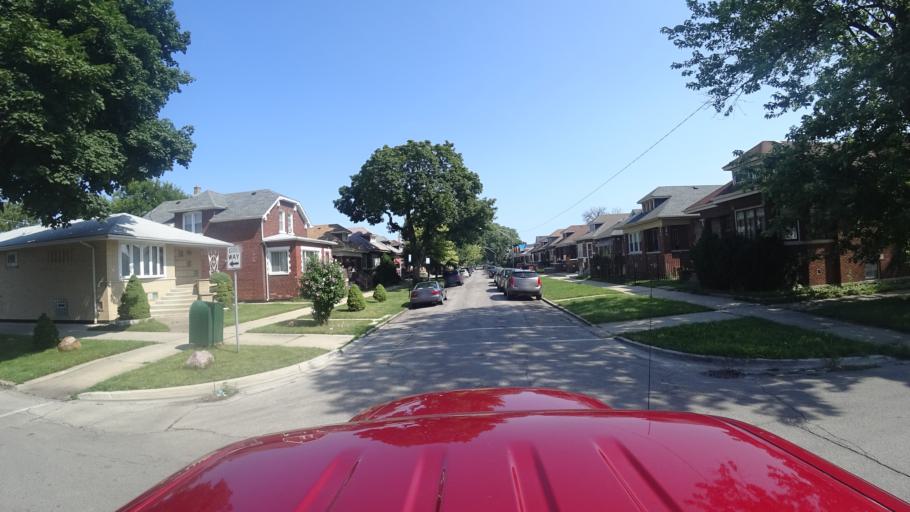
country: US
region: Illinois
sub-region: Cook County
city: Chicago
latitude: 41.7902
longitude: -87.6876
